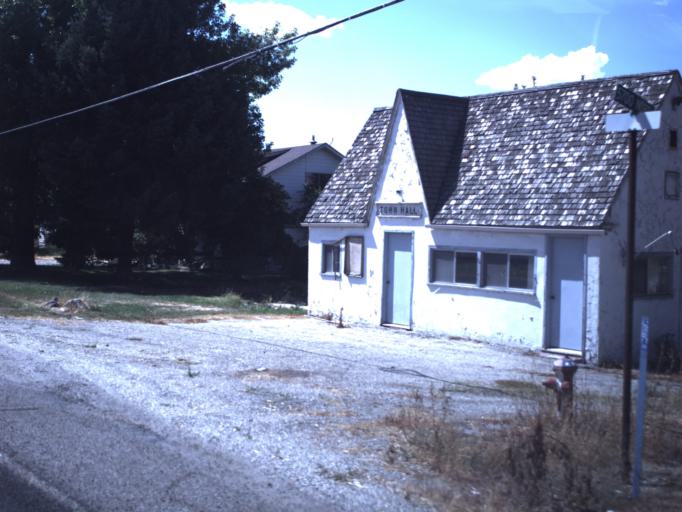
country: US
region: Utah
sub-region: Box Elder County
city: Honeyville
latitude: 41.6123
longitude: -112.1271
